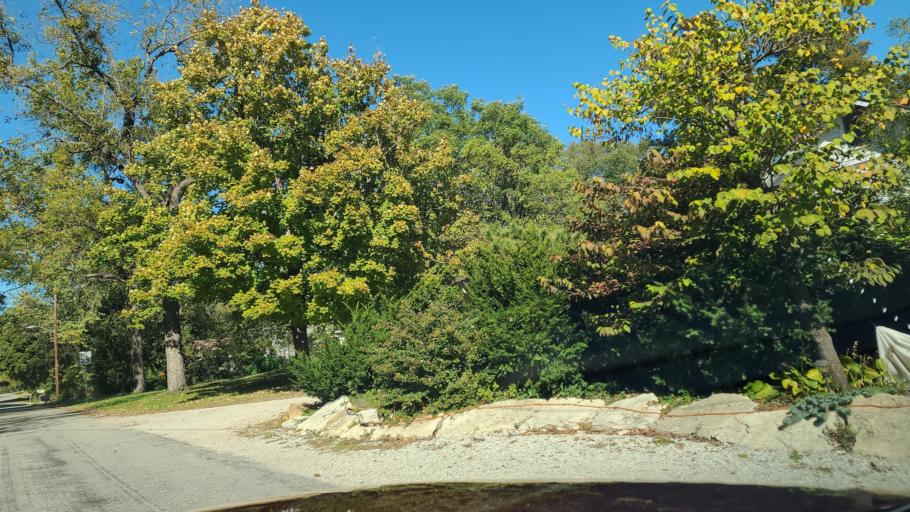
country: US
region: Kansas
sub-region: Douglas County
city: Lawrence
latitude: 38.9502
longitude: -95.2306
